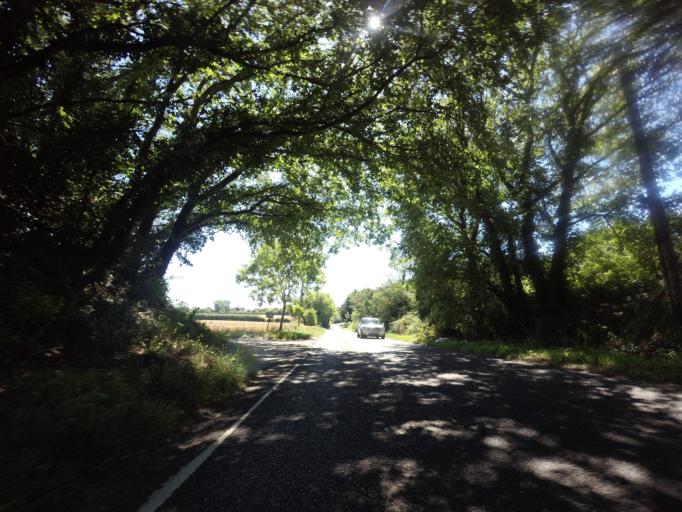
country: GB
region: England
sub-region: Kent
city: Ash
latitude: 51.2722
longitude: 1.2950
